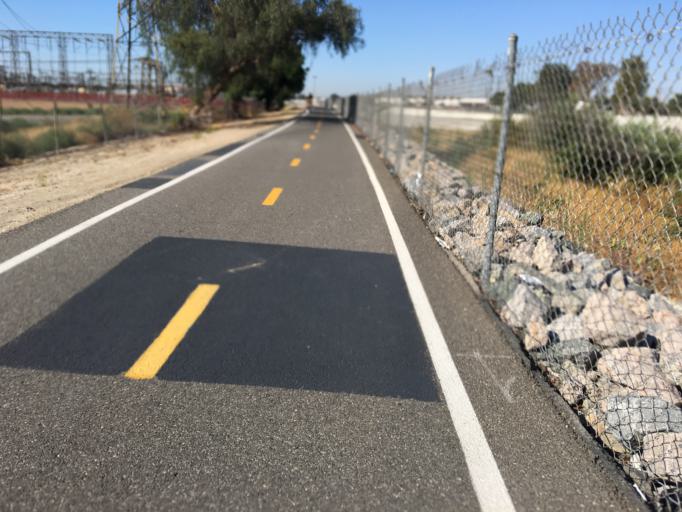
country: US
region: California
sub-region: Los Angeles County
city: Santa Fe Springs
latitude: 33.9320
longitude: -118.1060
